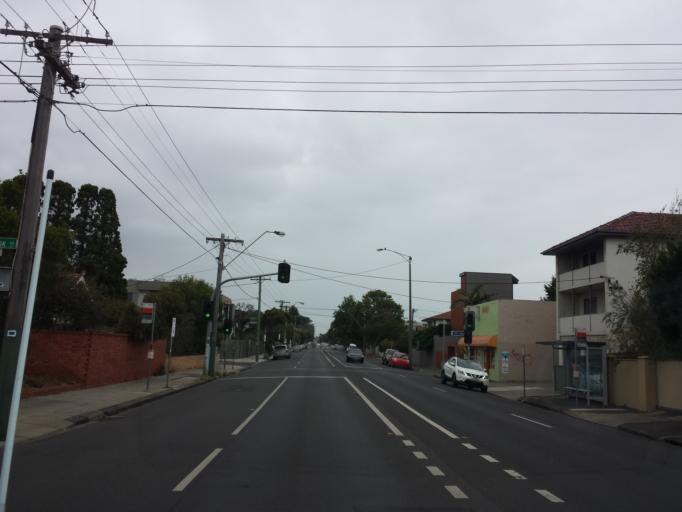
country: AU
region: Victoria
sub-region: Port Phillip
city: Balaclava
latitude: -37.8737
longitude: 144.9986
